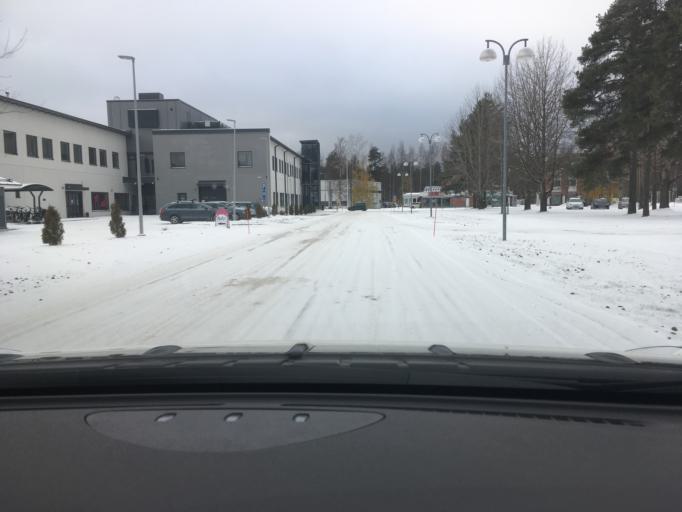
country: FI
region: North Karelia
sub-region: Joensuu
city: Joensuu
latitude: 62.6122
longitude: 29.7756
